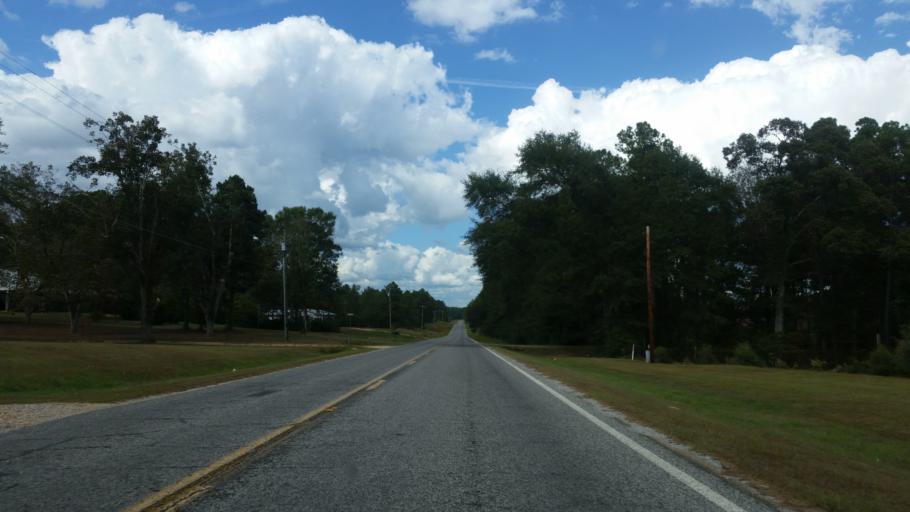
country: US
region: Mississippi
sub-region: Stone County
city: Wiggins
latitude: 30.8873
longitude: -89.1168
